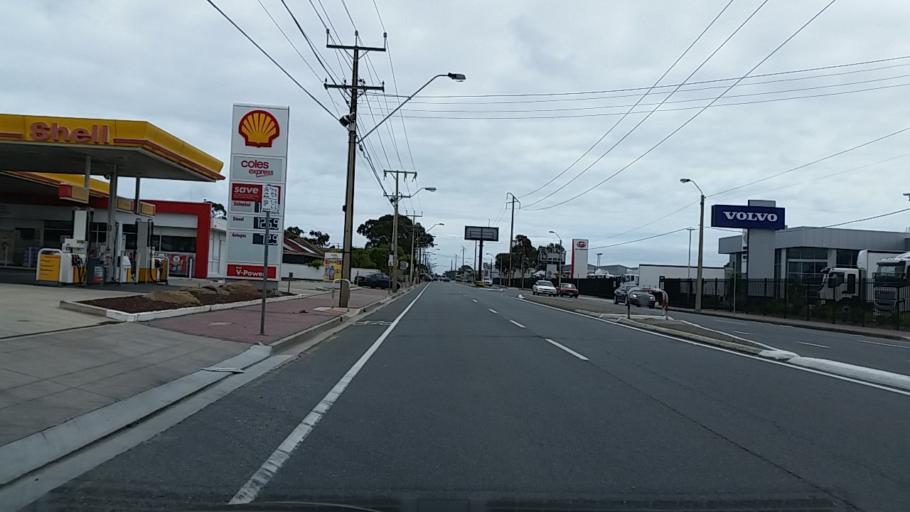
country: AU
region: South Australia
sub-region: Charles Sturt
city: Woodville North
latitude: -34.8502
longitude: 138.5551
